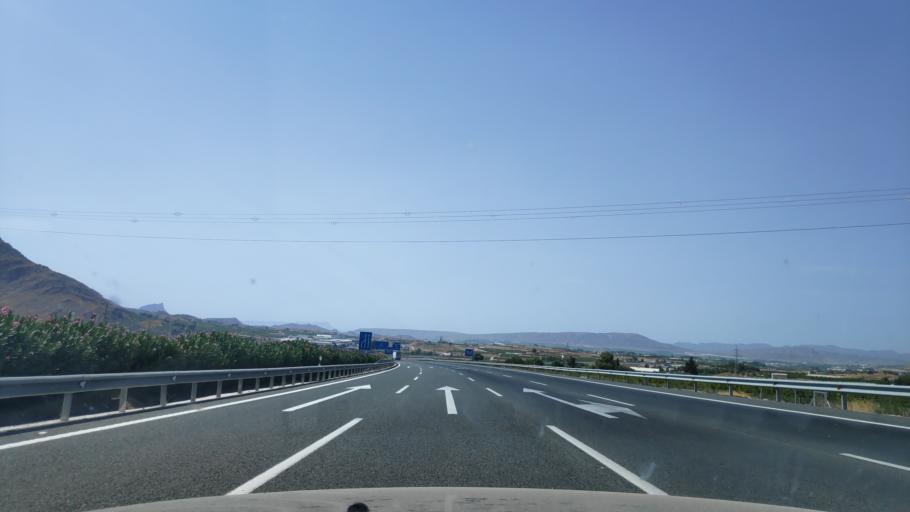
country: ES
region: Murcia
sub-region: Murcia
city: Ojos
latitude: 38.1822
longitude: -1.3180
